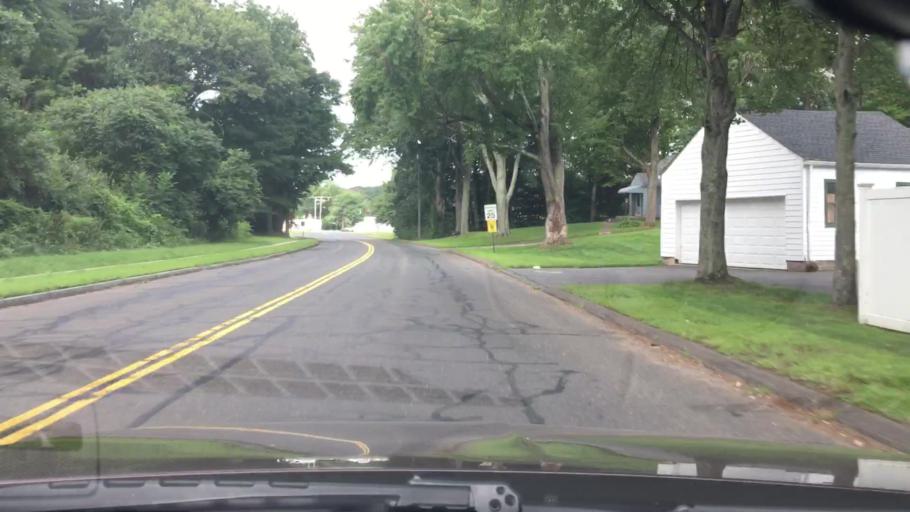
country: US
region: Connecticut
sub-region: Tolland County
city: Rockville
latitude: 41.8307
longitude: -72.4922
